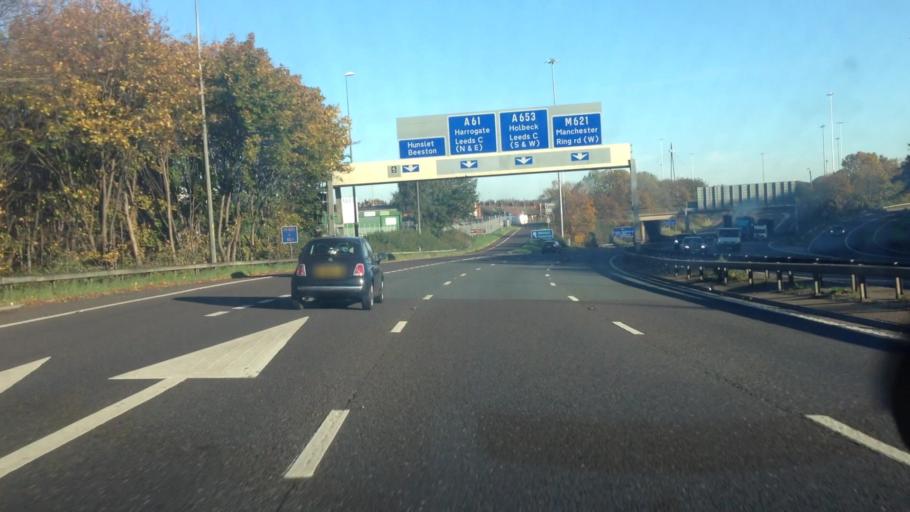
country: GB
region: England
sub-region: City and Borough of Leeds
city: Leeds
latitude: 53.7739
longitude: -1.5403
